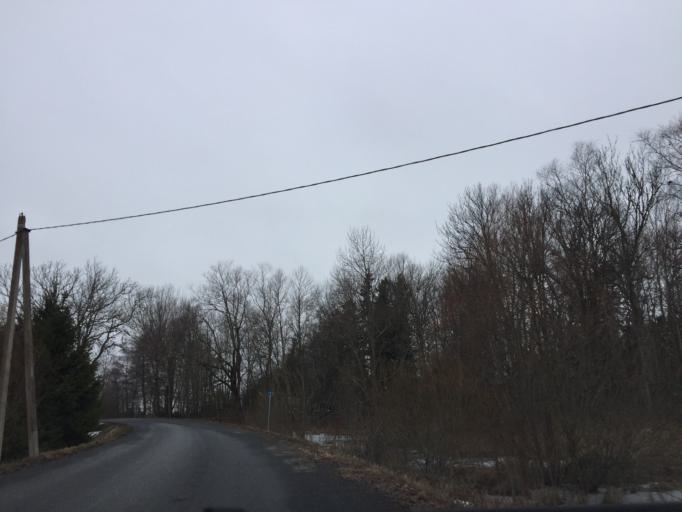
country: EE
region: Laeaene
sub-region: Haapsalu linn
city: Haapsalu
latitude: 58.7808
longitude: 23.4686
